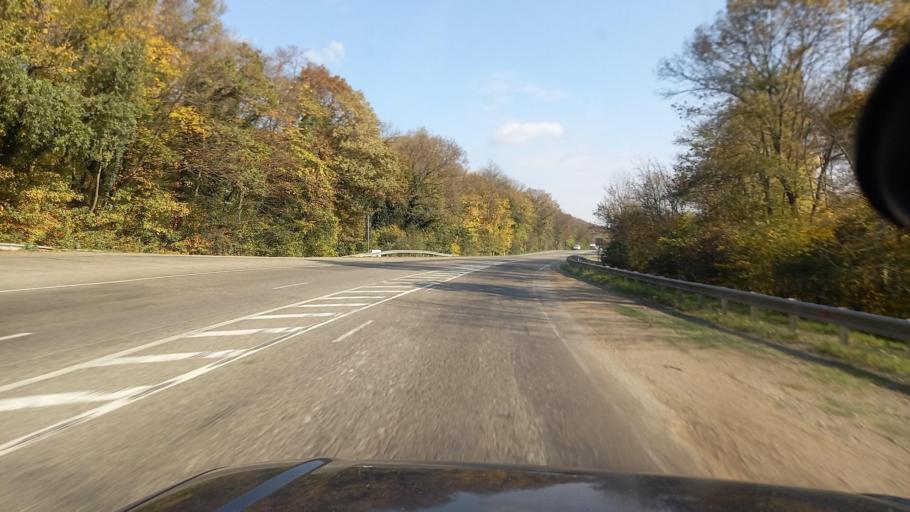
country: RU
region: Krasnodarskiy
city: Verkhnebakanskiy
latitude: 44.8470
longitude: 37.7198
